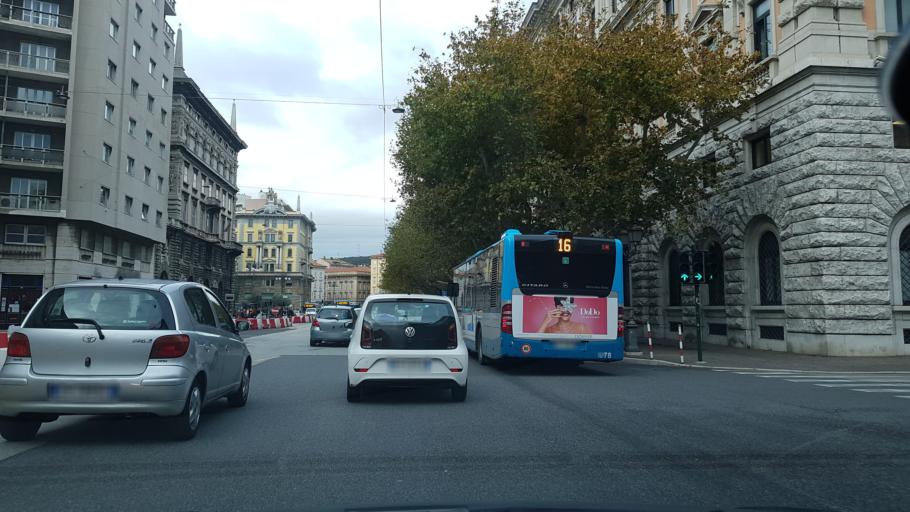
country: IT
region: Friuli Venezia Giulia
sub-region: Provincia di Trieste
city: Trieste
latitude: 45.6530
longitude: 13.7765
